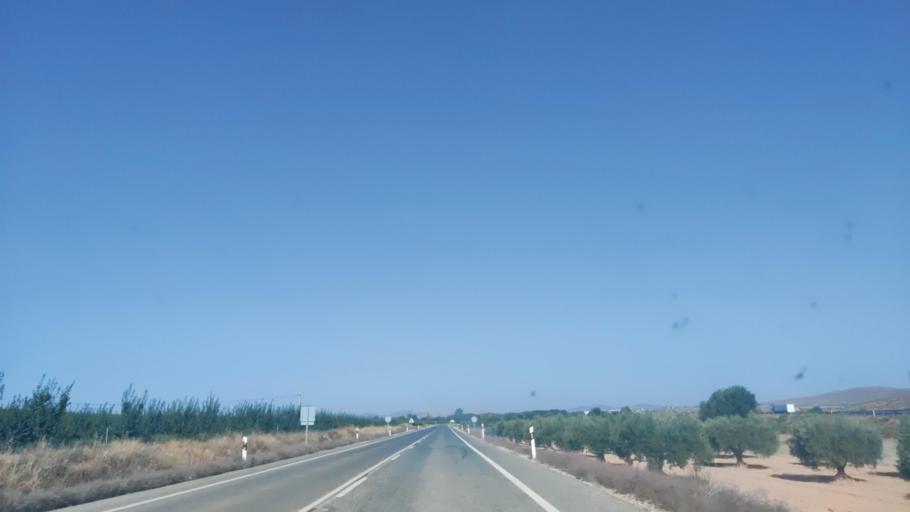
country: ES
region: Castille-La Mancha
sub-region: Provincia de Albacete
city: Hellin
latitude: 38.4929
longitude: -1.6307
